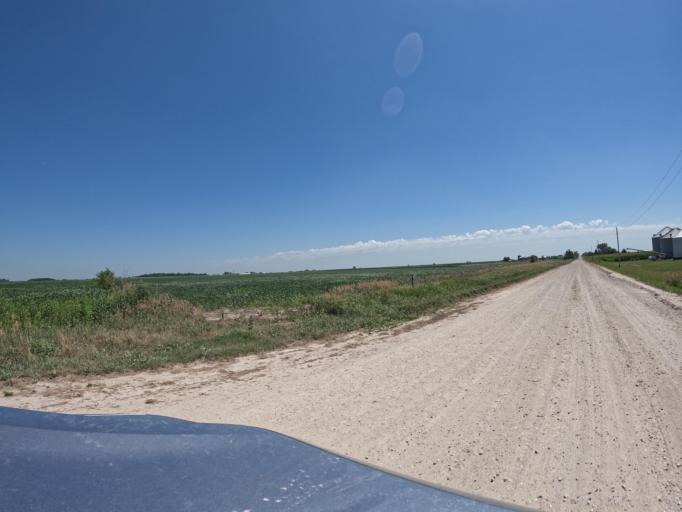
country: US
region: Iowa
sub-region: Poweshiek County
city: Montezuma
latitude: 41.4775
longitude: -92.3936
